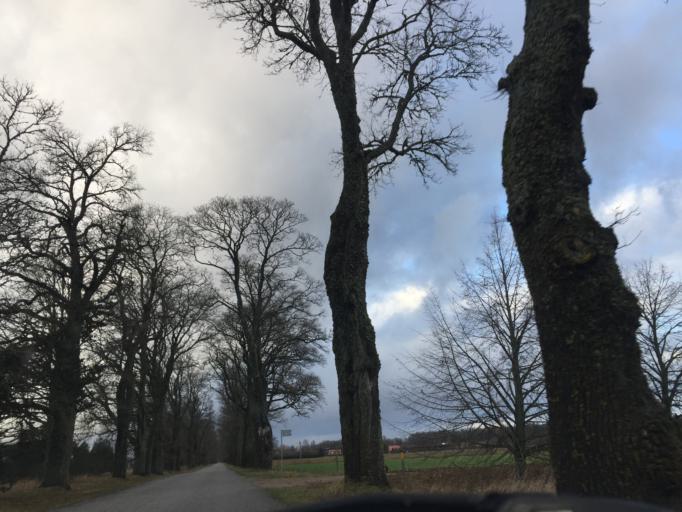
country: LV
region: Burtnieki
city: Matisi
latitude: 57.6874
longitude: 25.2864
